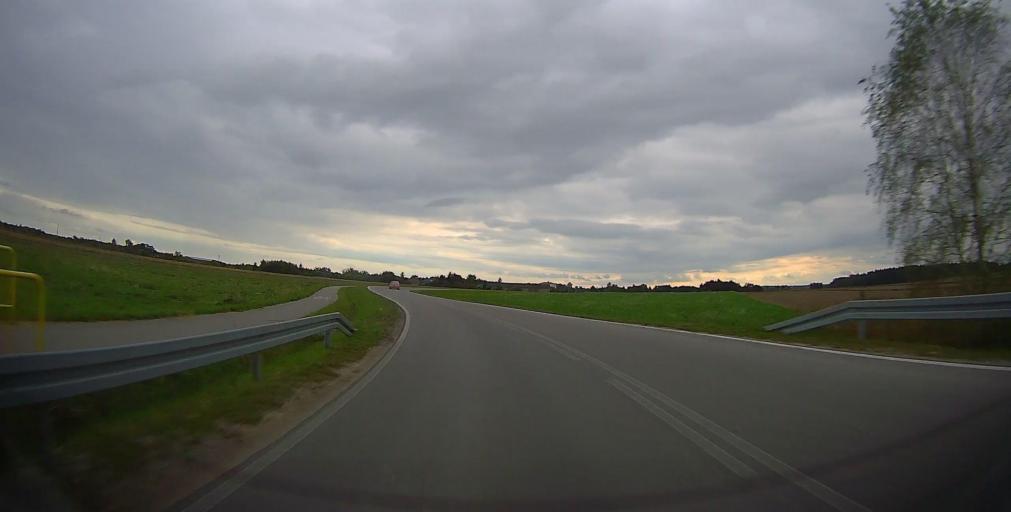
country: PL
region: Masovian Voivodeship
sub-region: Powiat radomski
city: Zakrzew
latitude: 51.4416
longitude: 21.0540
